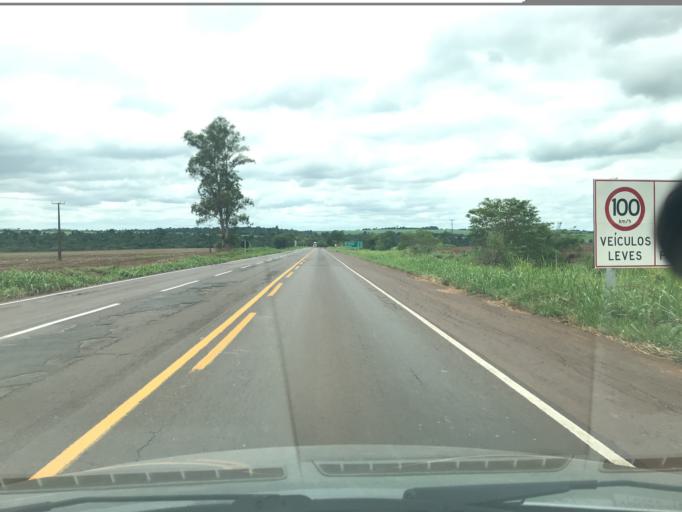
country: BR
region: Parana
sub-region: Terra Boa
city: Terra Boa
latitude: -23.6008
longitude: -52.3609
